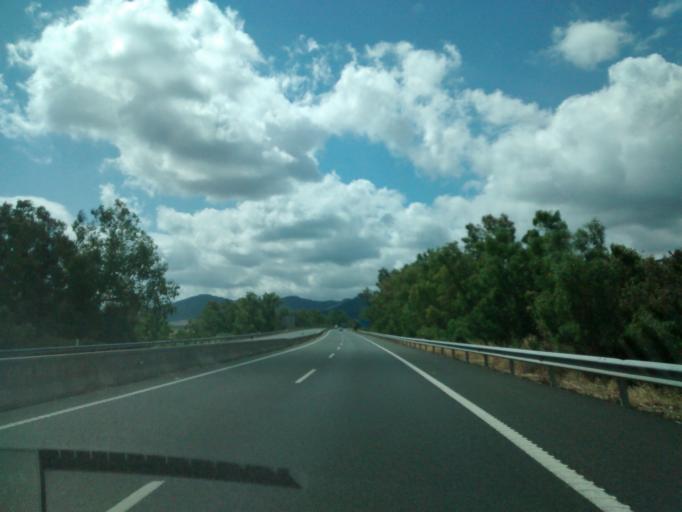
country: ES
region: Extremadura
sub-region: Provincia de Caceres
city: Romangordo
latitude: 39.7261
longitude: -5.7155
